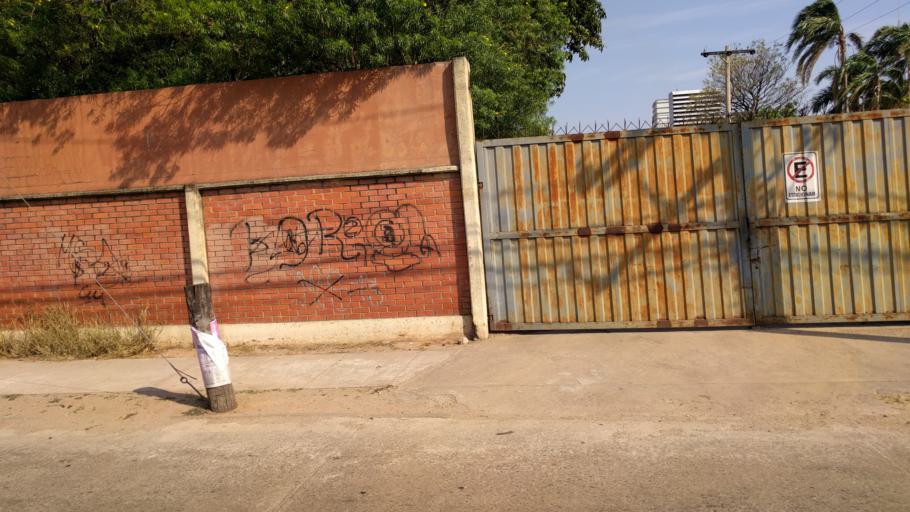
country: BO
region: Santa Cruz
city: Santa Cruz de la Sierra
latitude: -17.7857
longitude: -63.1531
